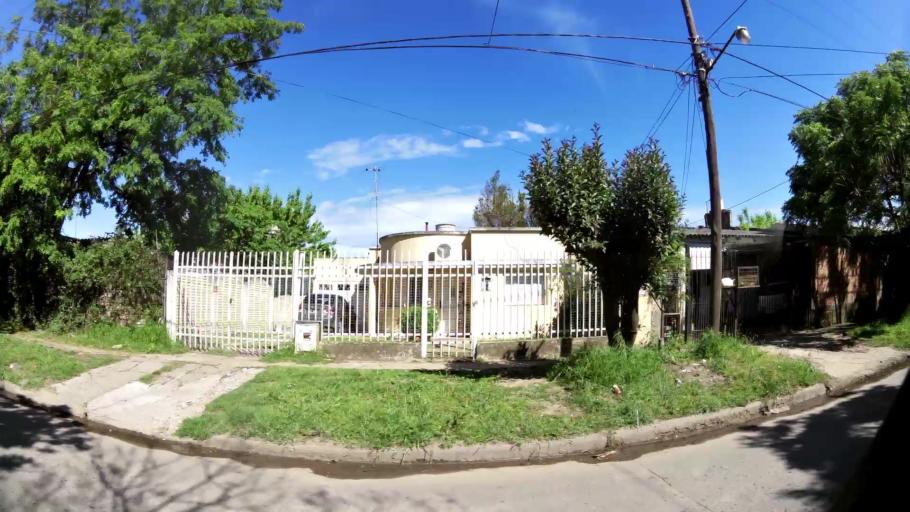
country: AR
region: Buenos Aires
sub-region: Partido de Almirante Brown
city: Adrogue
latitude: -34.7864
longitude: -58.3572
